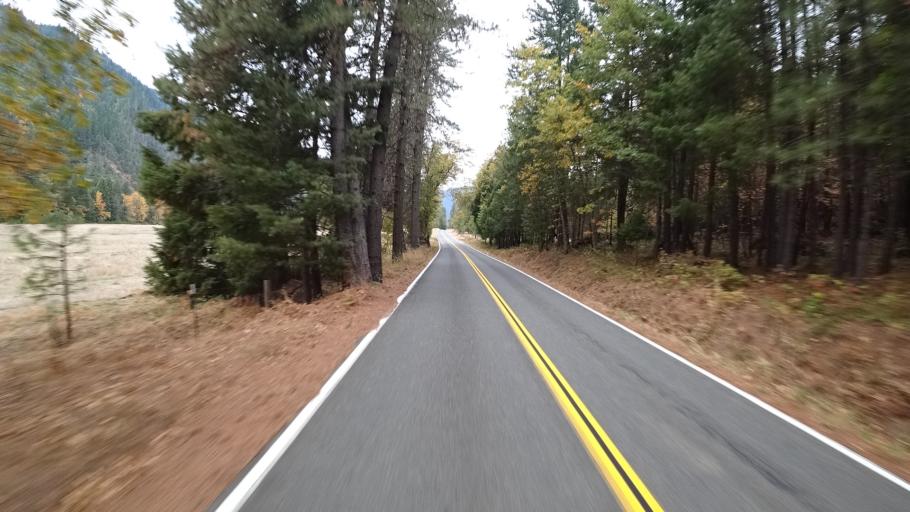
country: US
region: California
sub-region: Siskiyou County
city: Happy Camp
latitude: 41.8728
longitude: -123.4081
